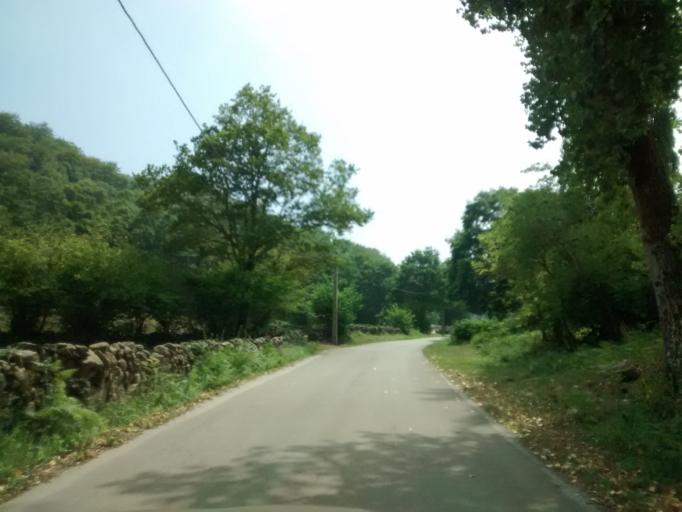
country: ES
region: Cantabria
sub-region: Provincia de Cantabria
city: Ruente
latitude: 43.2475
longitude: -4.2401
